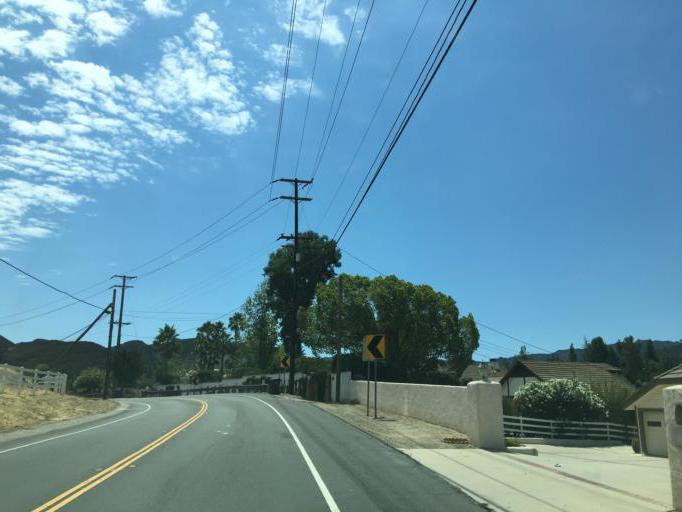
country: US
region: California
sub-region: Los Angeles County
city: Agoura
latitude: 34.1317
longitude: -118.7530
